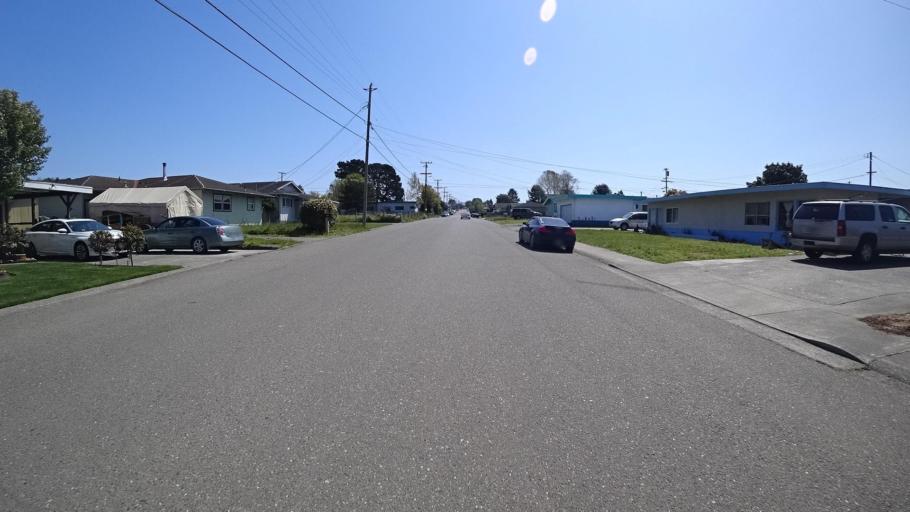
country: US
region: California
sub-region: Humboldt County
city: Fortuna
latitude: 40.5690
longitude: -124.1340
